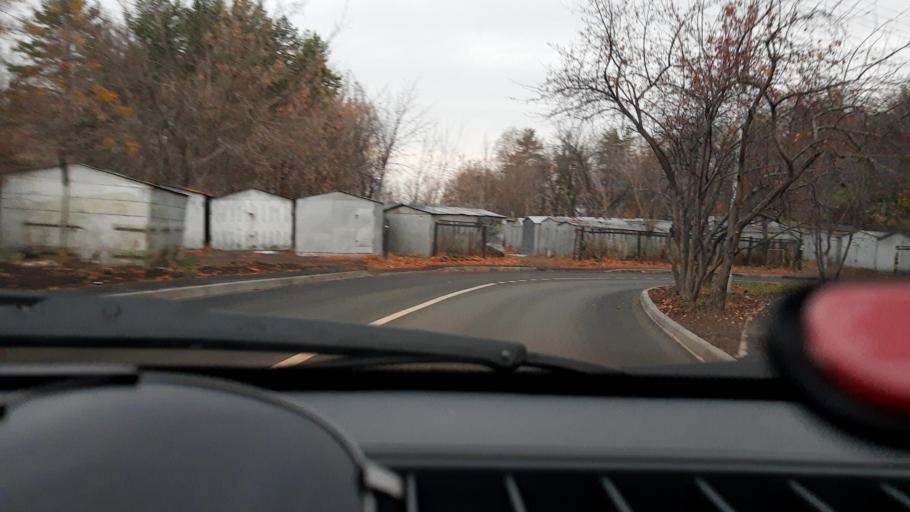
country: RU
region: Bashkortostan
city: Ufa
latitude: 54.7916
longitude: 56.0278
